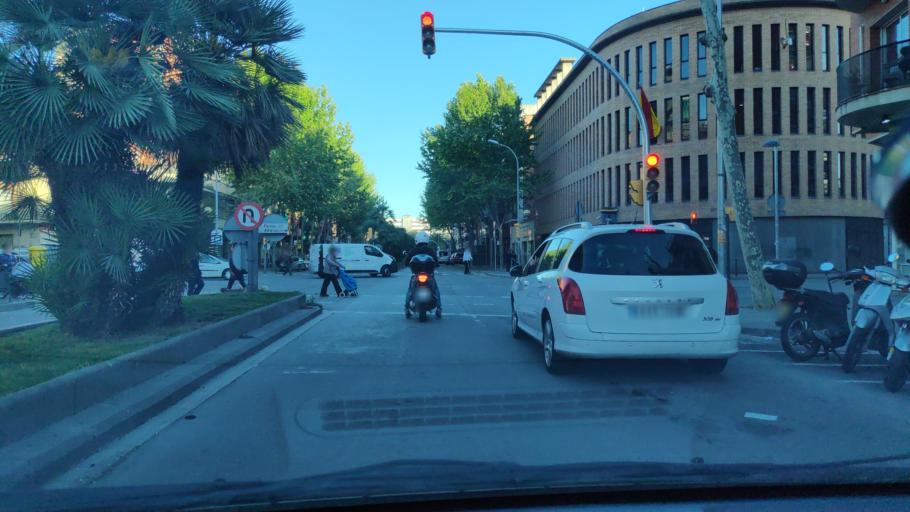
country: ES
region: Catalonia
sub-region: Provincia de Barcelona
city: Sant Adria de Besos
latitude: 41.4326
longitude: 2.2183
